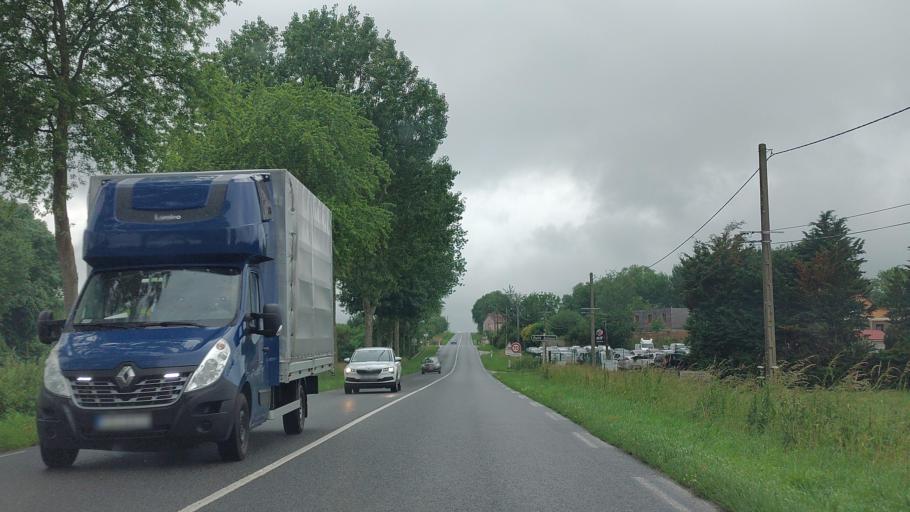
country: FR
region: Picardie
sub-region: Departement de la Somme
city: Chepy
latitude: 50.0870
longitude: 1.6704
